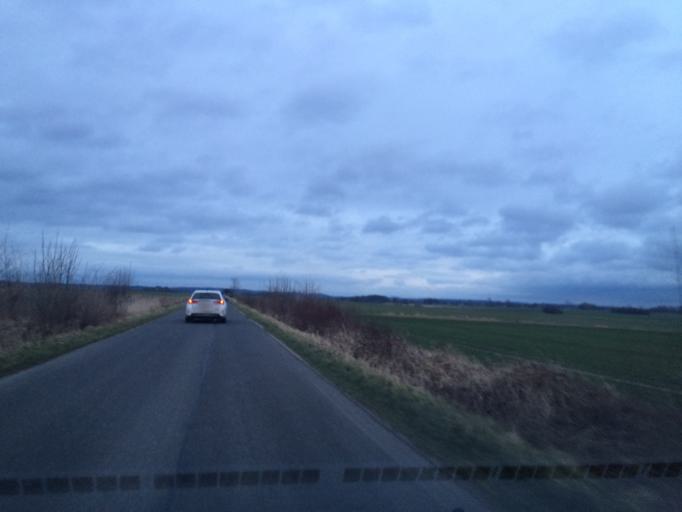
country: PL
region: Lower Silesian Voivodeship
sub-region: Powiat boleslawiecki
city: Nowogrodziec
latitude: 51.1979
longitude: 15.4618
